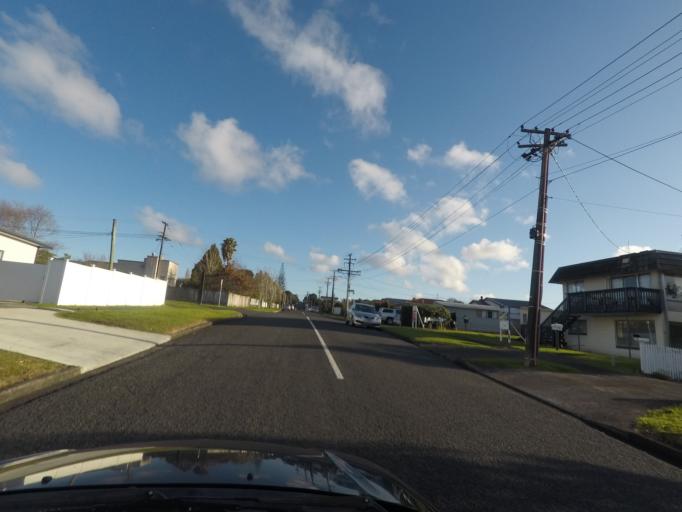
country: NZ
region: Auckland
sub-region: Auckland
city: Waitakere
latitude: -36.9005
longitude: 174.6717
